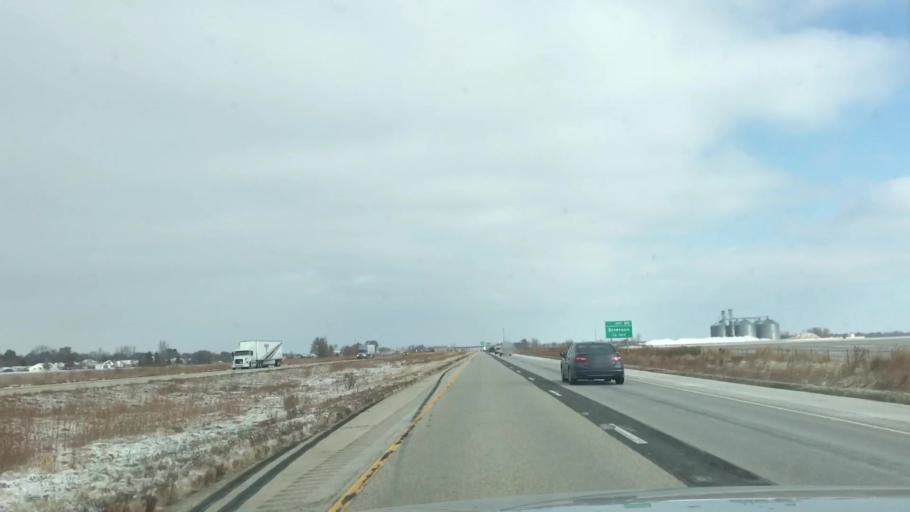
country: US
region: Illinois
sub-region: Sangamon County
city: Divernon
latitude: 39.5546
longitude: -89.6460
